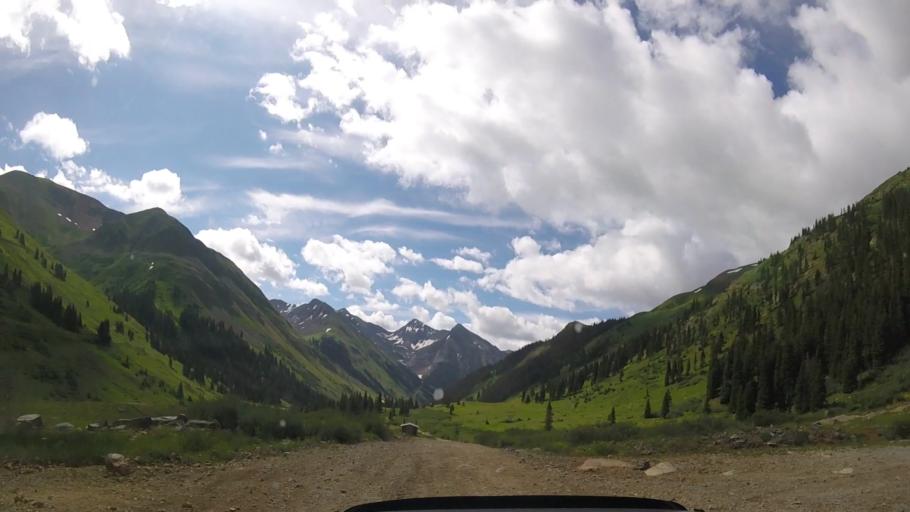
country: US
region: Colorado
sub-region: Ouray County
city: Ouray
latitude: 37.9306
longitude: -107.5702
